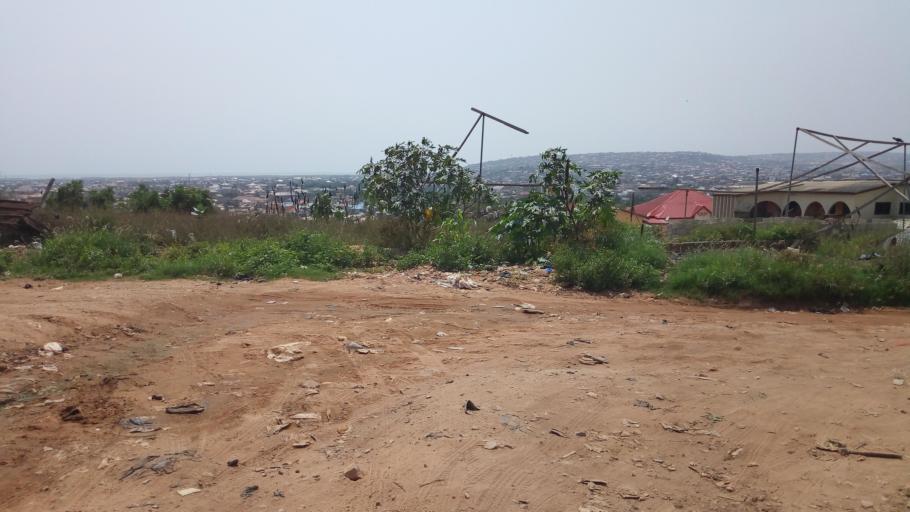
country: GH
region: Greater Accra
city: Gbawe
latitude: 5.5624
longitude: -0.3094
